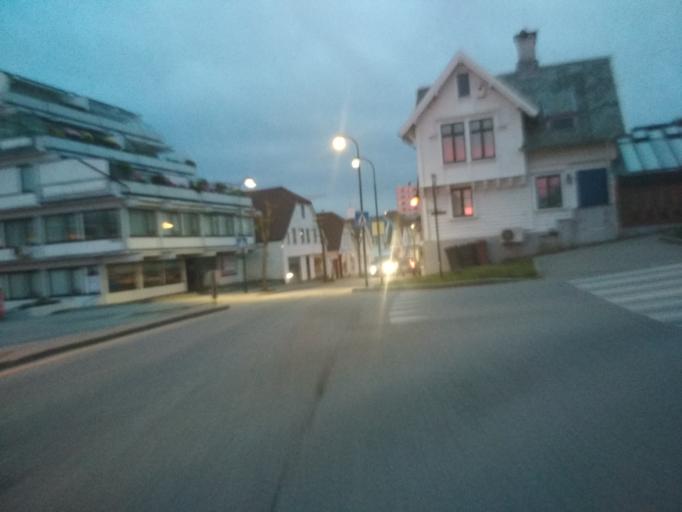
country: NO
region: Rogaland
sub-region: Stavanger
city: Stavanger
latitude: 58.9717
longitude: 5.7233
